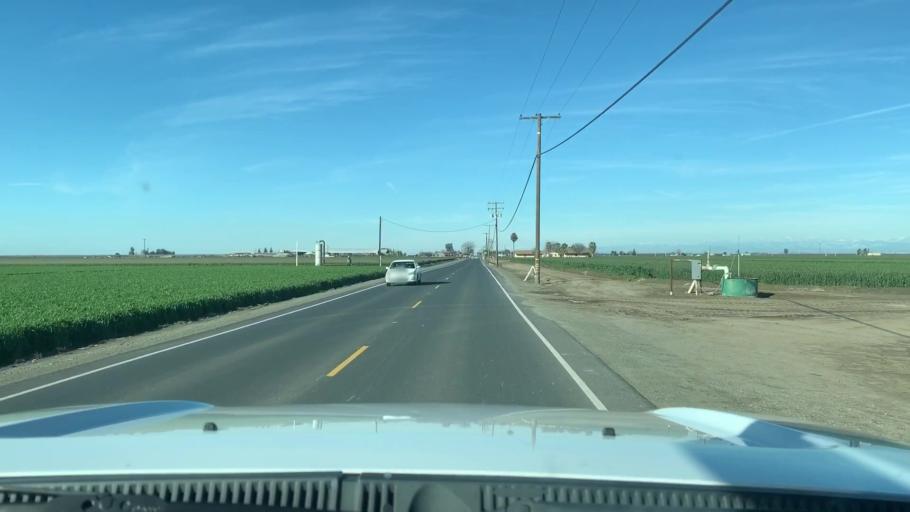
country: US
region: California
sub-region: Kings County
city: Corcoran
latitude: 36.1920
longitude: -119.4932
